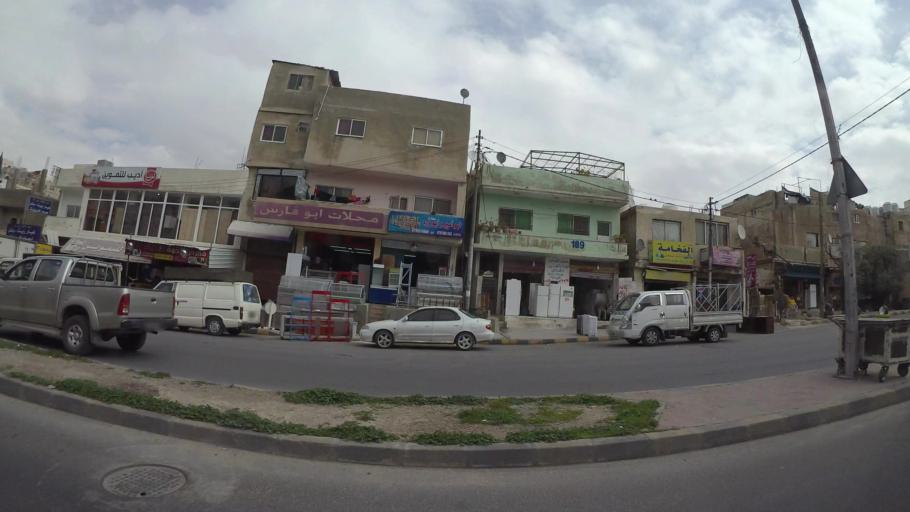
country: JO
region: Amman
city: Amman
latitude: 31.9646
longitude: 35.9307
